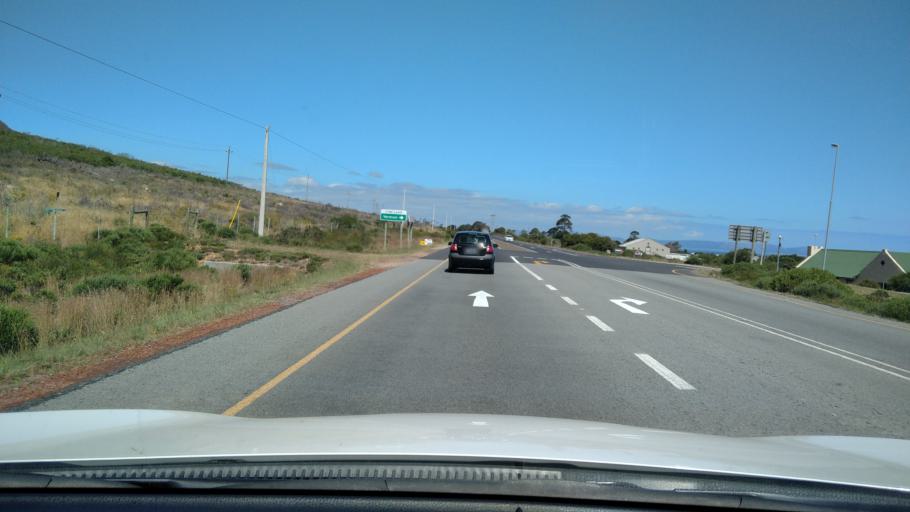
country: ZA
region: Western Cape
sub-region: Overberg District Municipality
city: Hermanus
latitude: -34.4052
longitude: 19.1481
